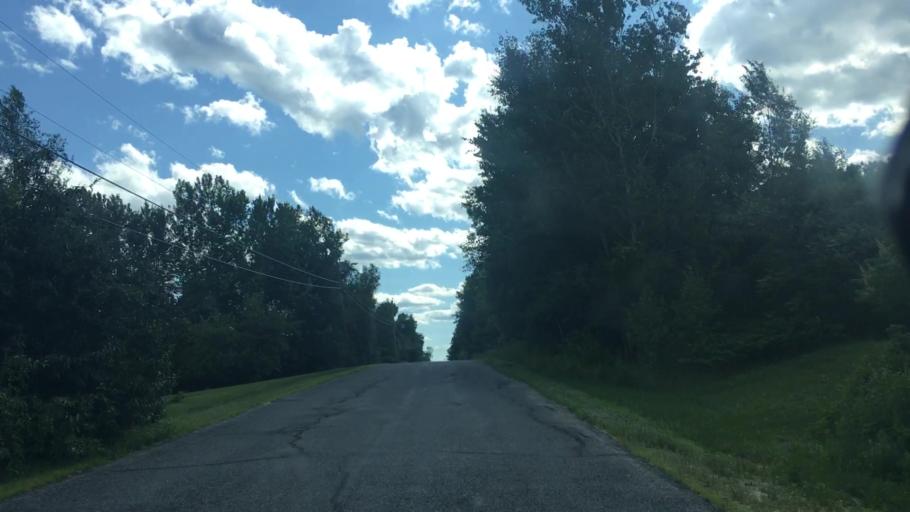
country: US
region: Maine
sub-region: Franklin County
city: Wilton
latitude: 44.6271
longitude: -70.2080
